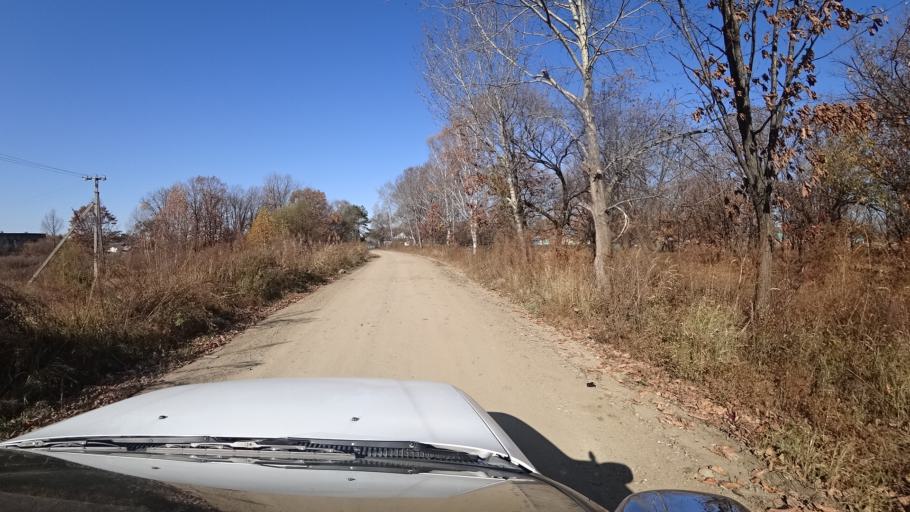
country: RU
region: Primorskiy
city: Dal'nerechensk
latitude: 45.9121
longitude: 133.8080
